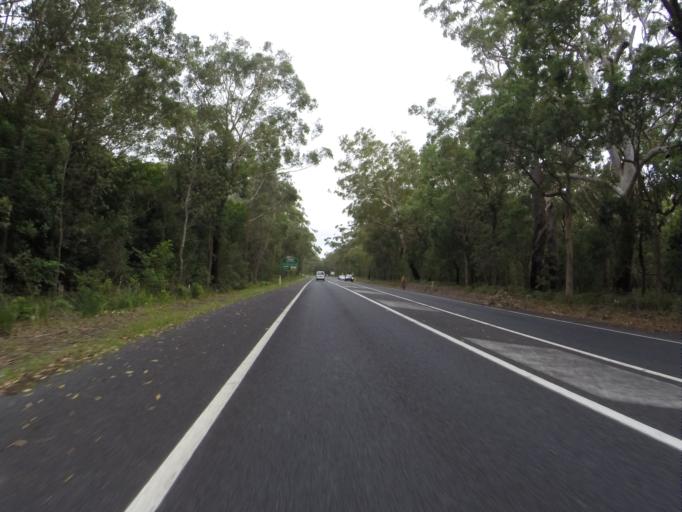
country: AU
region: New South Wales
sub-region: Kiama
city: Gerringong
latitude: -34.7919
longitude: 150.7731
